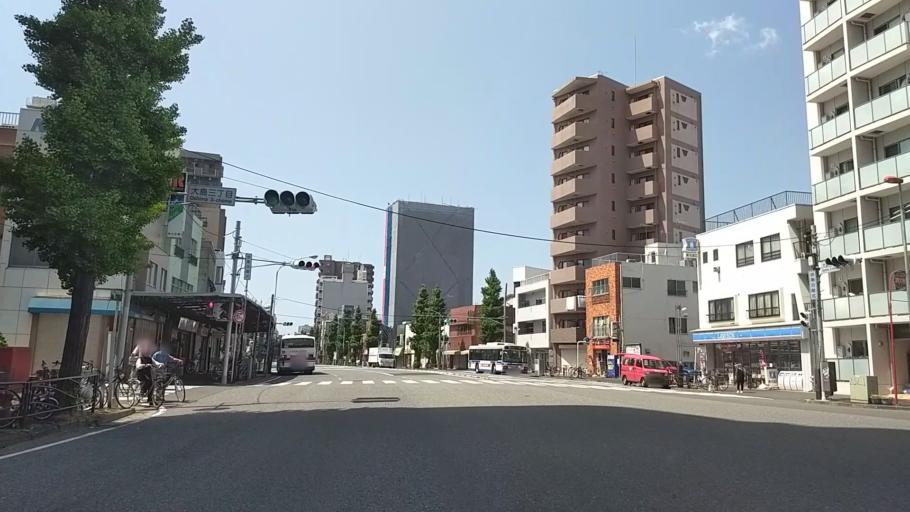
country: JP
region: Kanagawa
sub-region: Kawasaki-shi
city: Kawasaki
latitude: 35.5193
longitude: 139.7167
